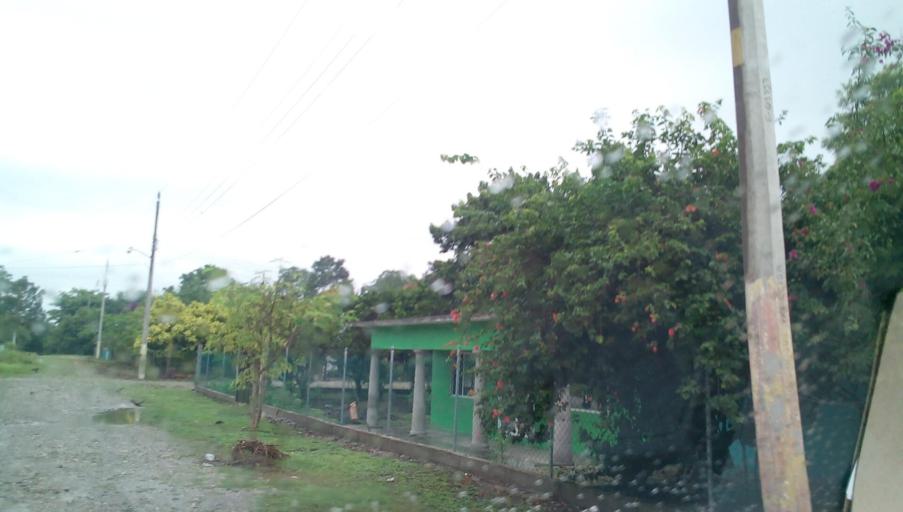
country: MX
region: Veracruz
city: Tempoal de Sanchez
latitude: 21.4199
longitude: -98.4264
